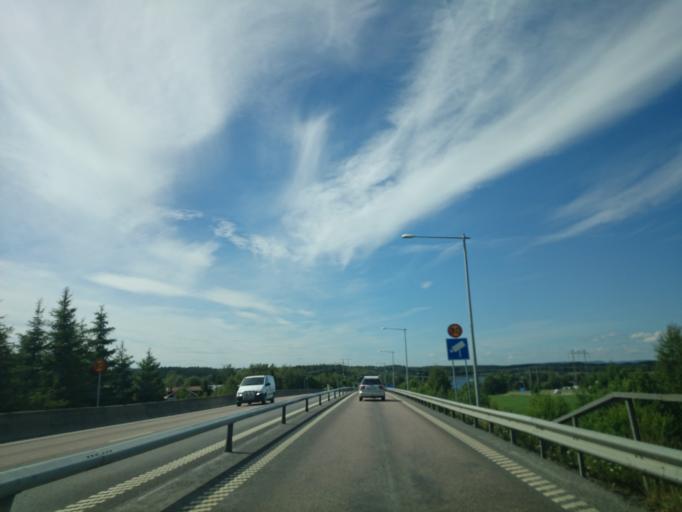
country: SE
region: Jaemtland
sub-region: Krokoms Kommun
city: Krokom
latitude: 63.3138
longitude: 14.4638
